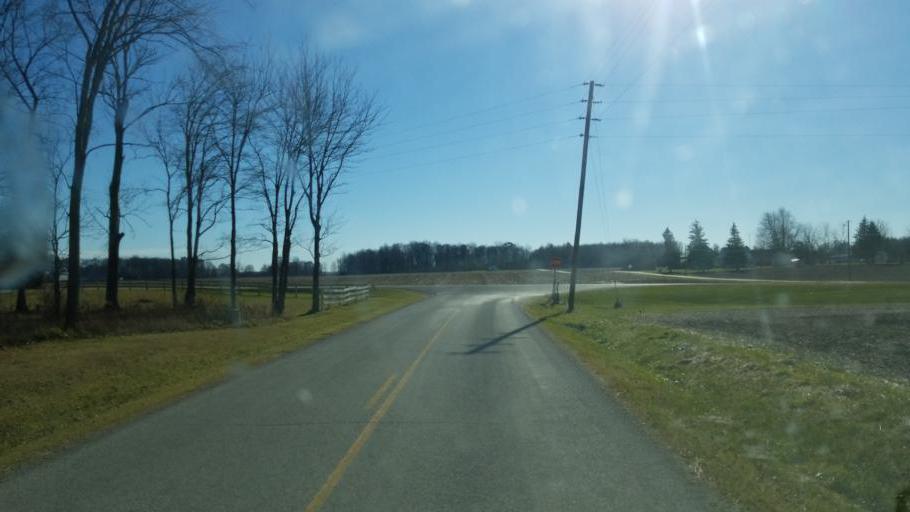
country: US
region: Ohio
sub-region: Crawford County
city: Galion
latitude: 40.8133
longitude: -82.8374
